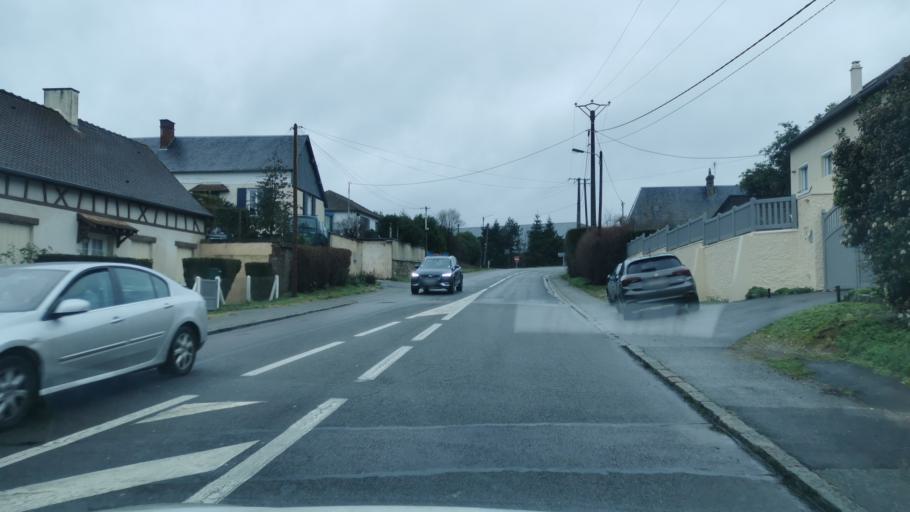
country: FR
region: Haute-Normandie
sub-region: Departement de l'Eure
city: Gravigny
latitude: 49.0673
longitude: 1.1728
